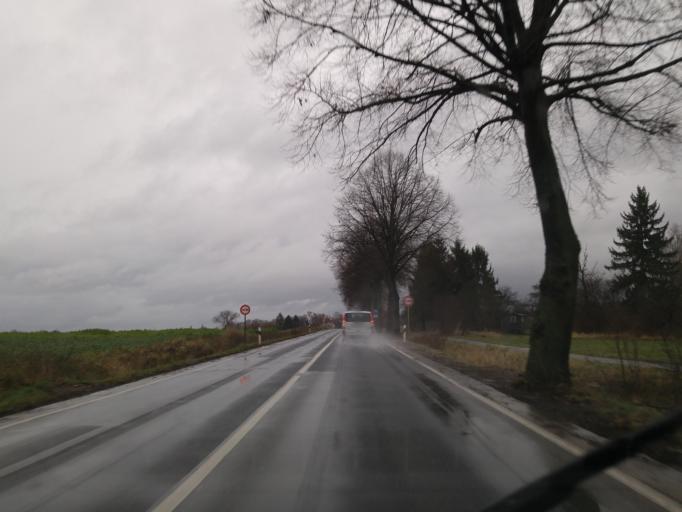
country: DE
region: Lower Saxony
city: Goettingen
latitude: 51.5050
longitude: 9.9381
